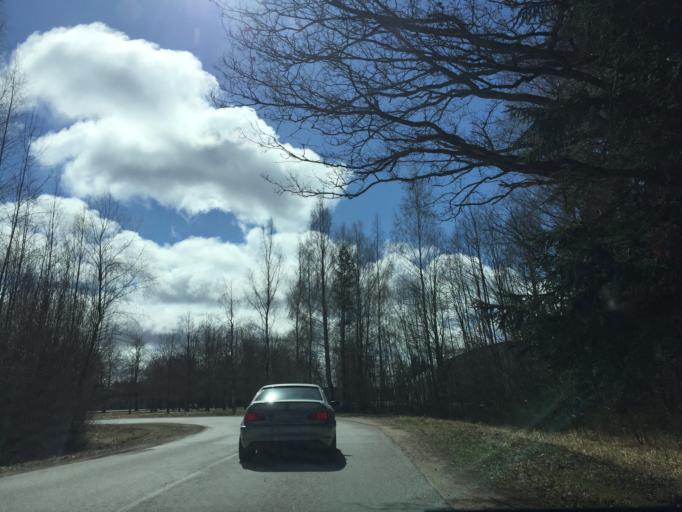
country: LV
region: Seja
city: Loja
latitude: 57.1472
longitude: 24.6775
